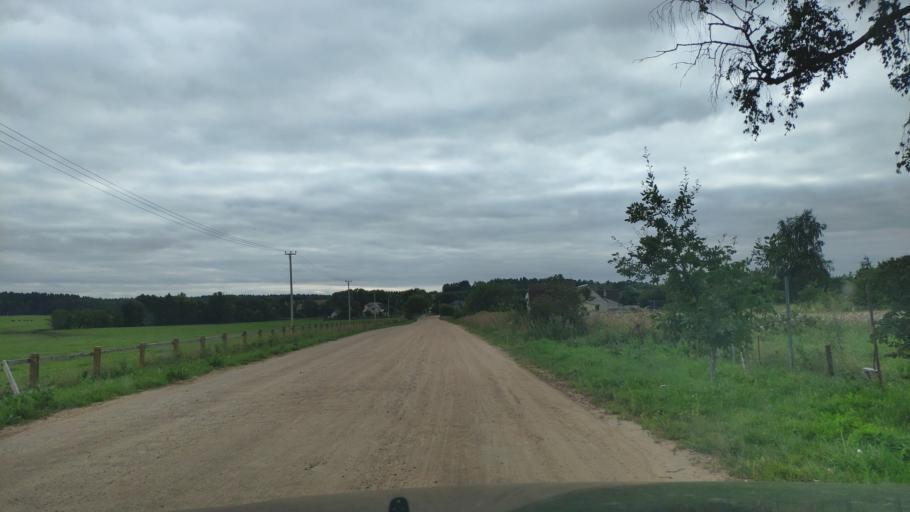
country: BY
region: Minsk
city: Khatsyezhyna
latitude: 53.9290
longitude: 27.2651
